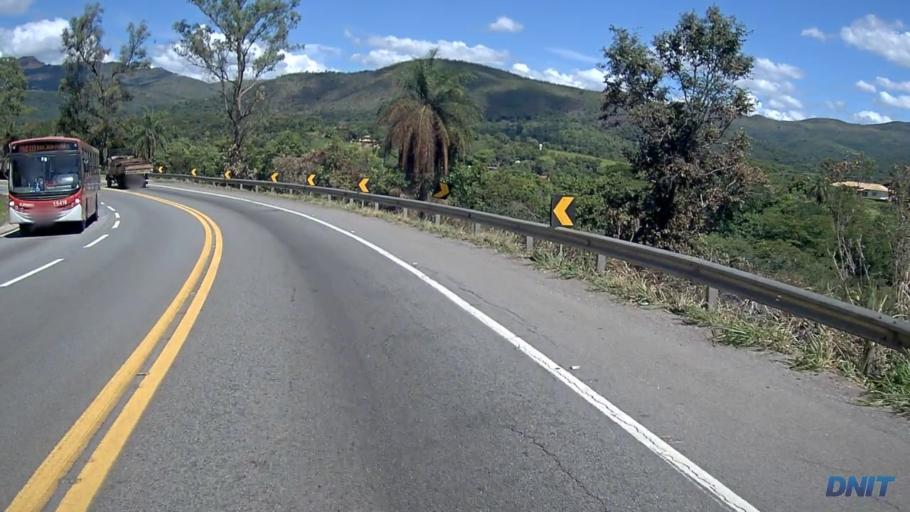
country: BR
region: Minas Gerais
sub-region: Santa Luzia
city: Santa Luzia
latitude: -19.7999
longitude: -43.7595
